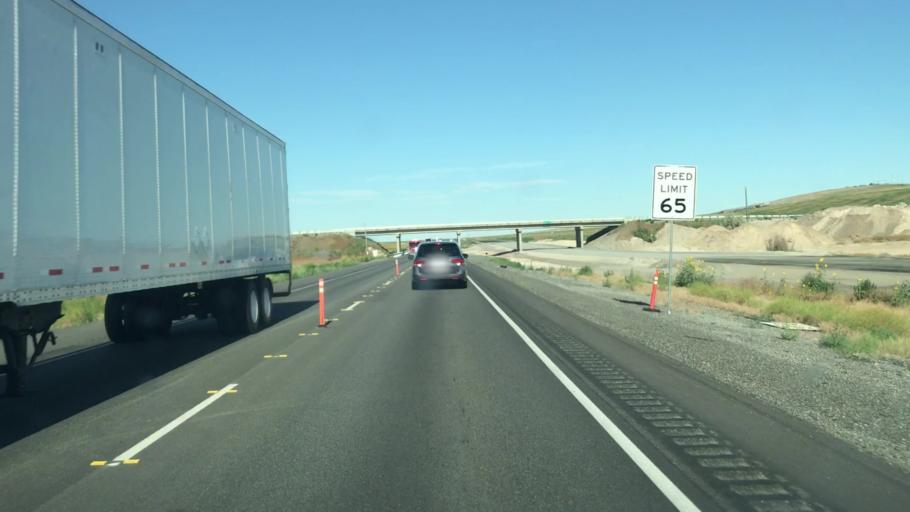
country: US
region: Idaho
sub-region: Twin Falls County
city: Hansen
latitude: 42.5759
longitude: -114.2078
